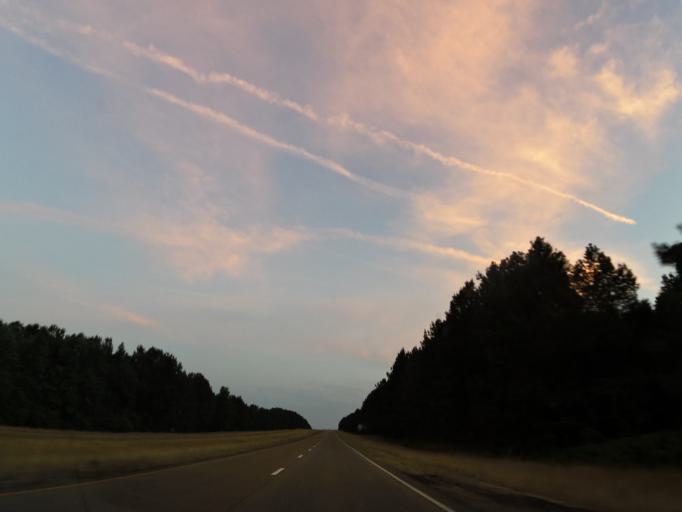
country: US
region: Mississippi
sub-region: Lauderdale County
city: Meridian Station
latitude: 32.5861
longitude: -88.5022
